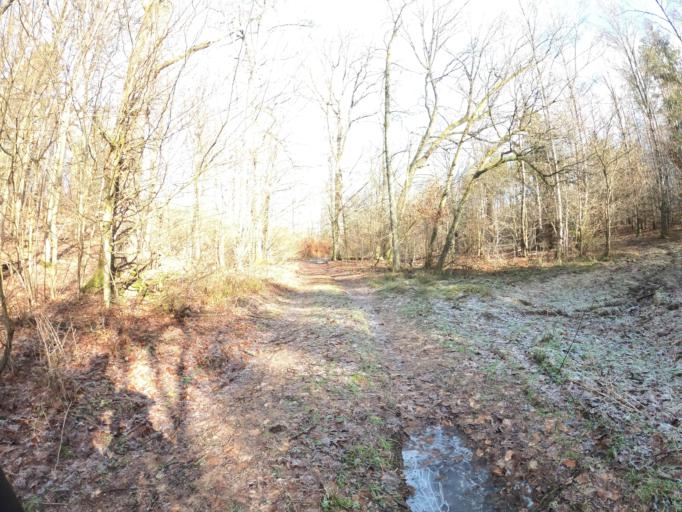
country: PL
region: West Pomeranian Voivodeship
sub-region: Powiat koszalinski
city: Polanow
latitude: 54.1254
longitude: 16.7686
